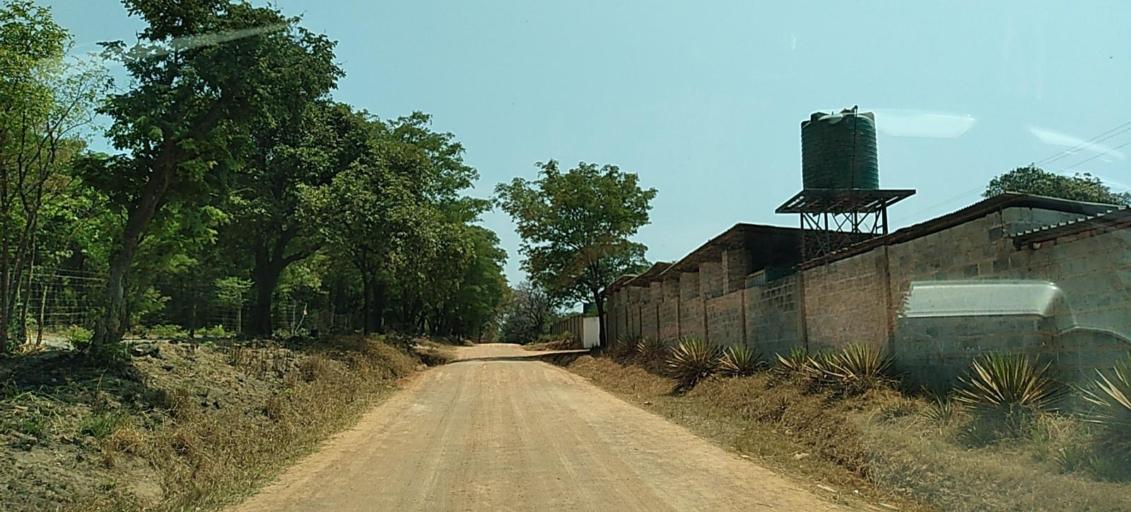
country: ZM
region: Copperbelt
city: Chambishi
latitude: -12.6077
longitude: 27.9531
